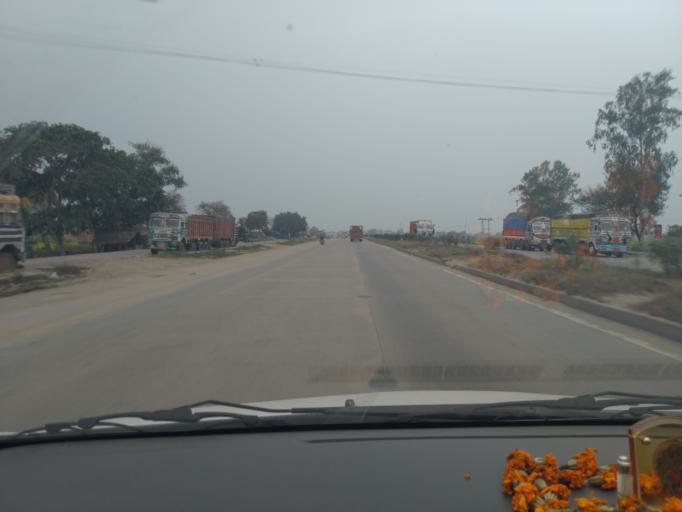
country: IN
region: Bihar
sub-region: Rohtas
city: Dehri
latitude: 24.9728
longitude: 83.9099
